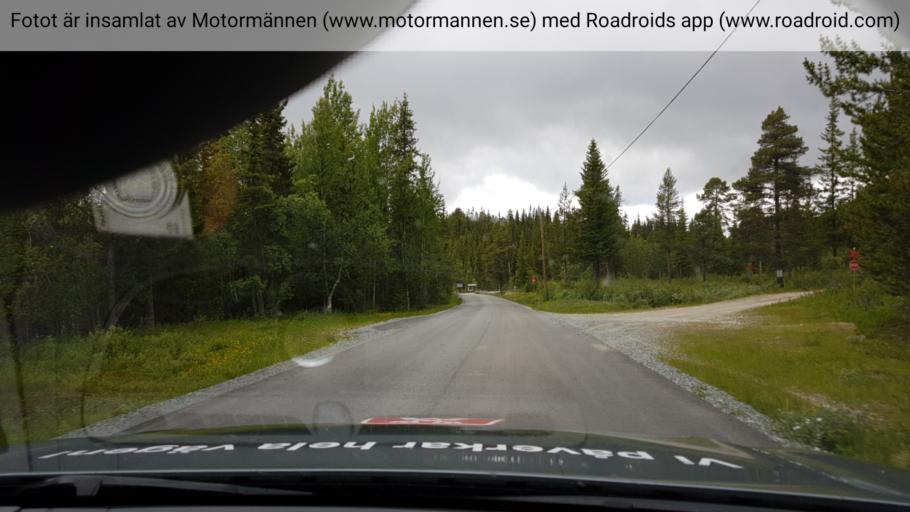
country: SE
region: Jaemtland
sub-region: Are Kommun
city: Are
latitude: 62.8603
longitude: 12.7661
